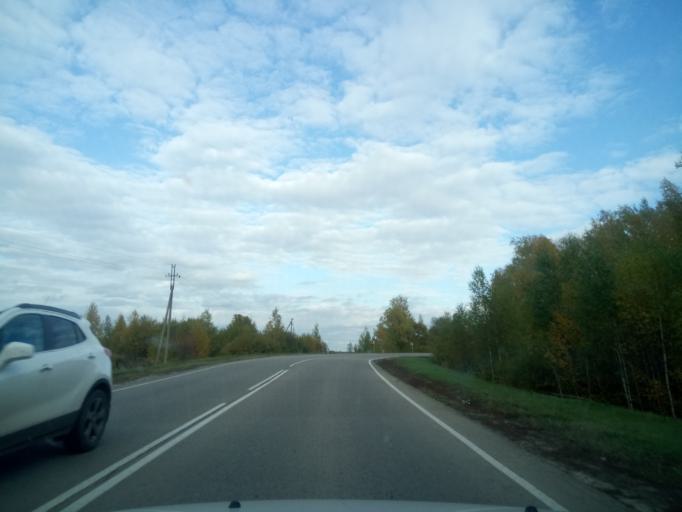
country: RU
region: Nizjnij Novgorod
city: Bol'shoye Boldino
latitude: 54.9224
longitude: 45.1429
